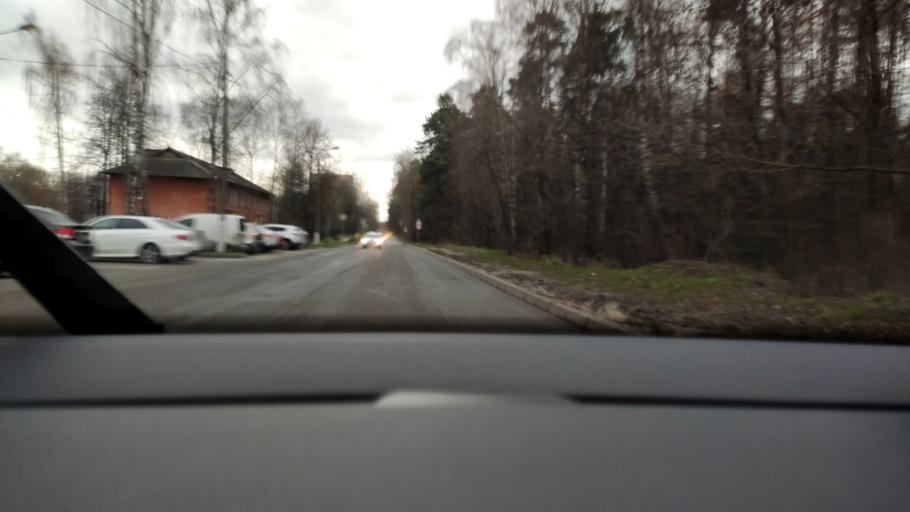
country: RU
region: Moskovskaya
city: Balashikha
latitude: 55.8155
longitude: 37.9484
